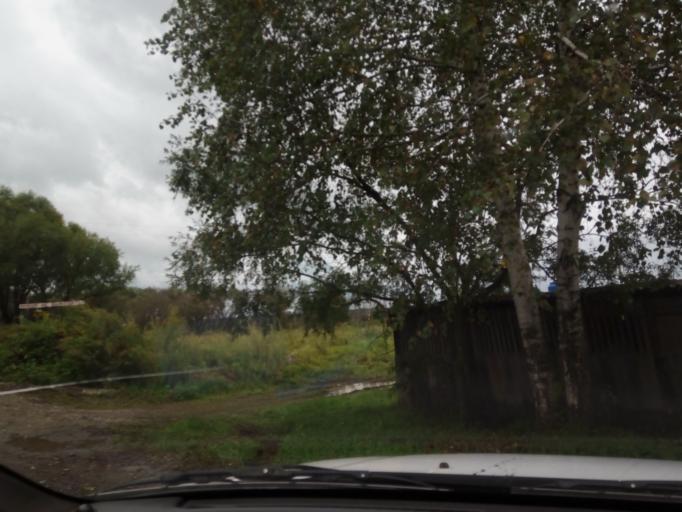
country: RU
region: Primorskiy
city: Dal'nerechensk
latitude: 45.9161
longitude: 133.7248
